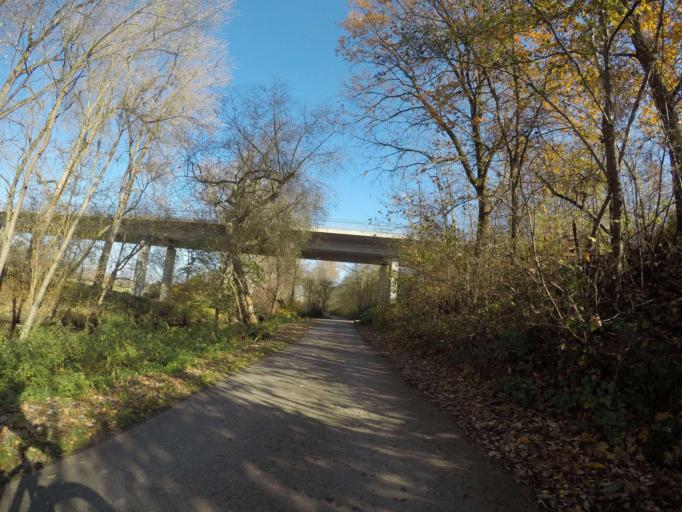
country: DE
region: Baden-Wuerttemberg
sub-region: Tuebingen Region
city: Riedlingen
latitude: 48.1545
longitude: 9.4888
